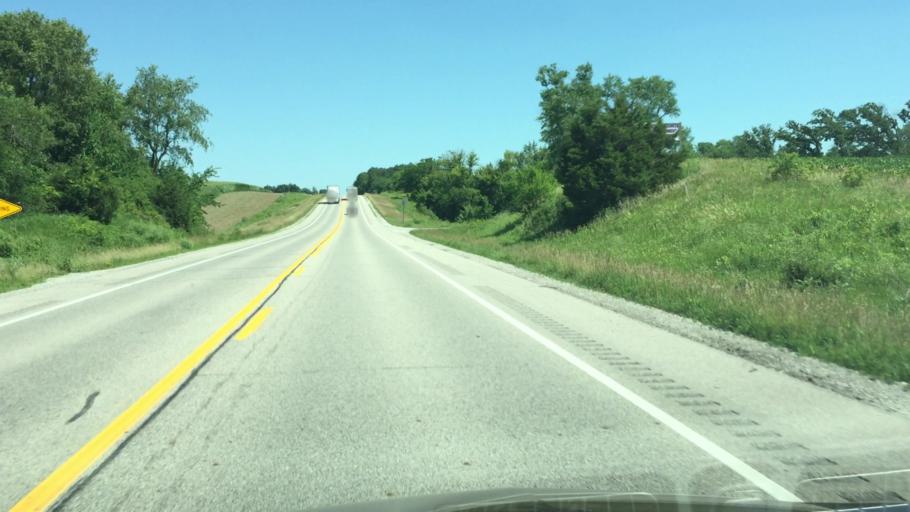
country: US
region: Iowa
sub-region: Johnson County
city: Solon
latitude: 41.7687
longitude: -91.4829
